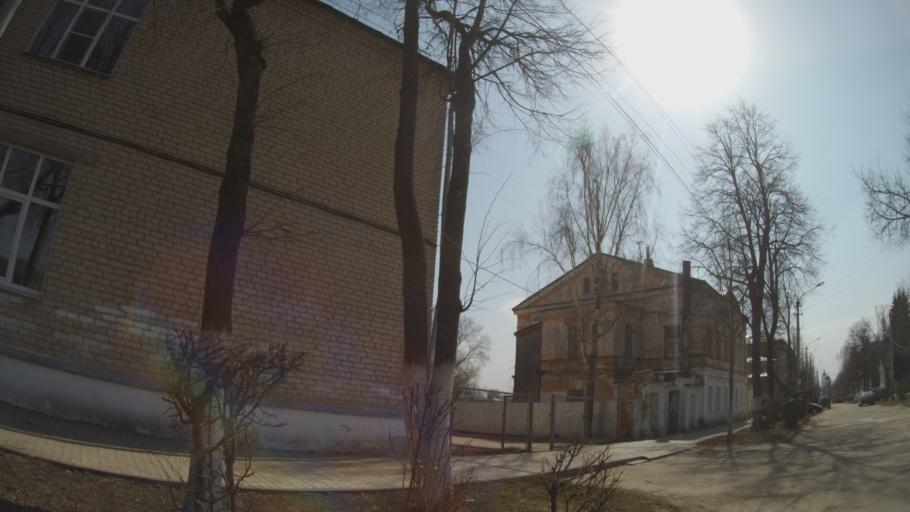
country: RU
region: Nizjnij Novgorod
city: Arzamas
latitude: 55.3893
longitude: 43.8178
